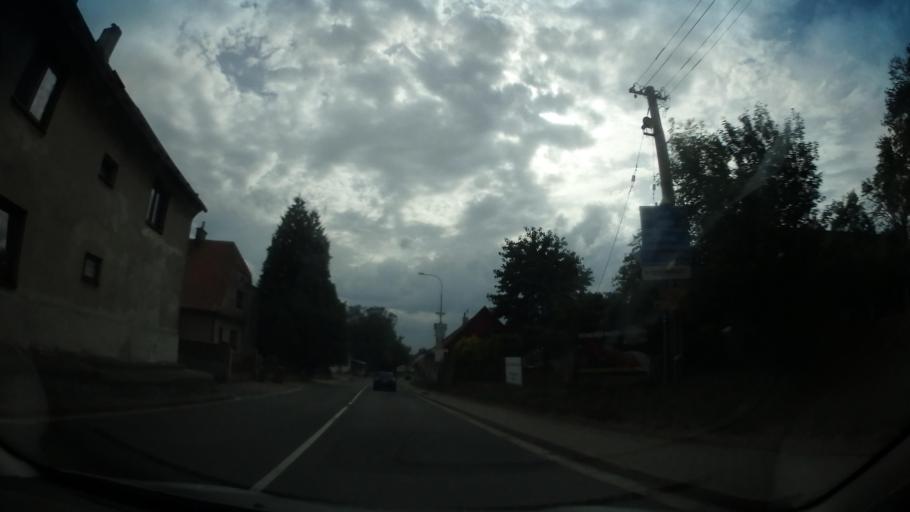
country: CZ
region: Pardubicky
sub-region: Okres Chrudim
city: Sec
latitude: 49.8482
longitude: 15.6620
